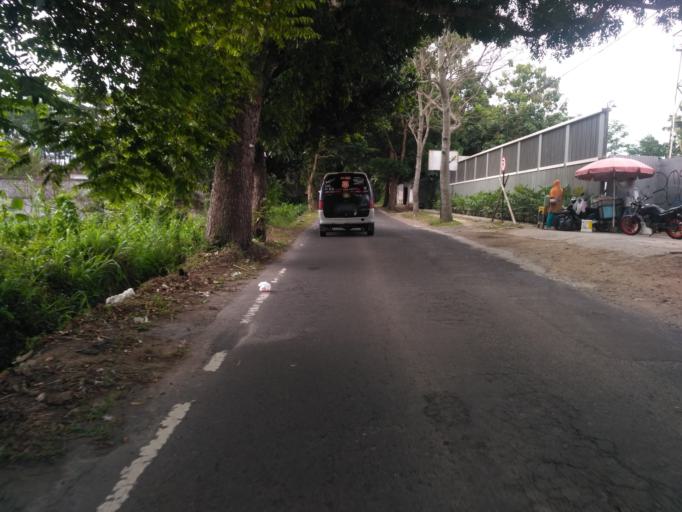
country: ID
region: Daerah Istimewa Yogyakarta
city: Melati
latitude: -7.7362
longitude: 110.3527
